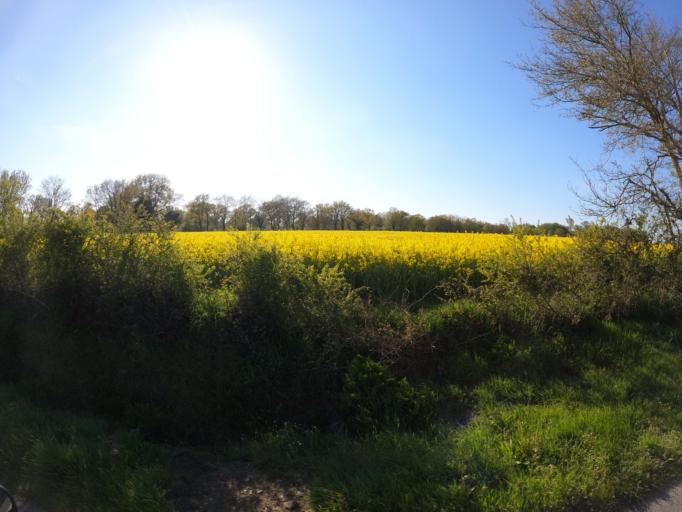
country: FR
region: Pays de la Loire
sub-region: Departement de la Vendee
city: Beaurepaire
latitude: 46.9185
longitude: -1.1222
